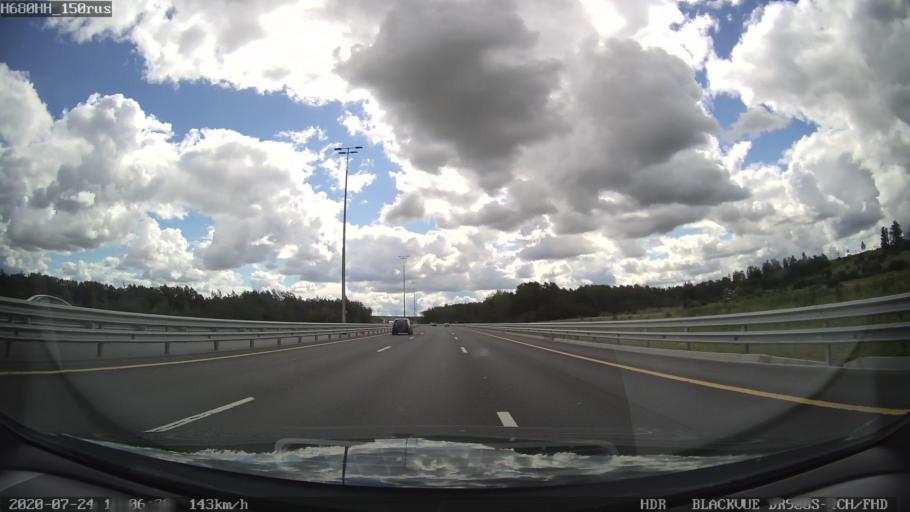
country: RU
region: St.-Petersburg
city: Shushary
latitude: 59.7643
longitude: 30.3729
